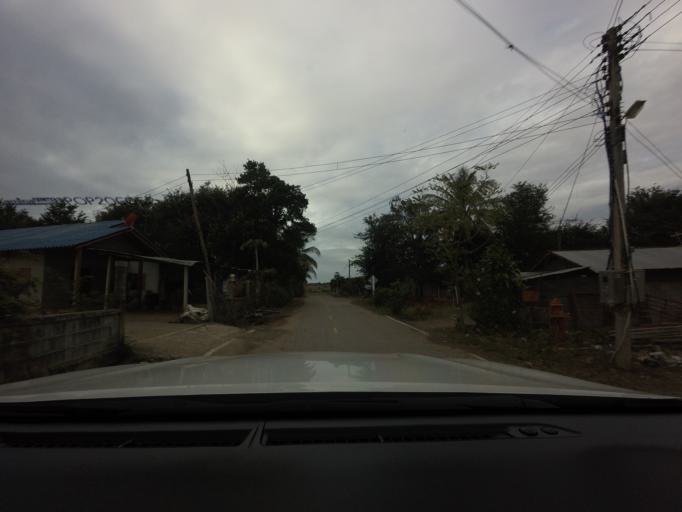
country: TH
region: Nakhon Ratchasima
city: Wang Nam Khiao
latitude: 14.4670
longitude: 101.6599
